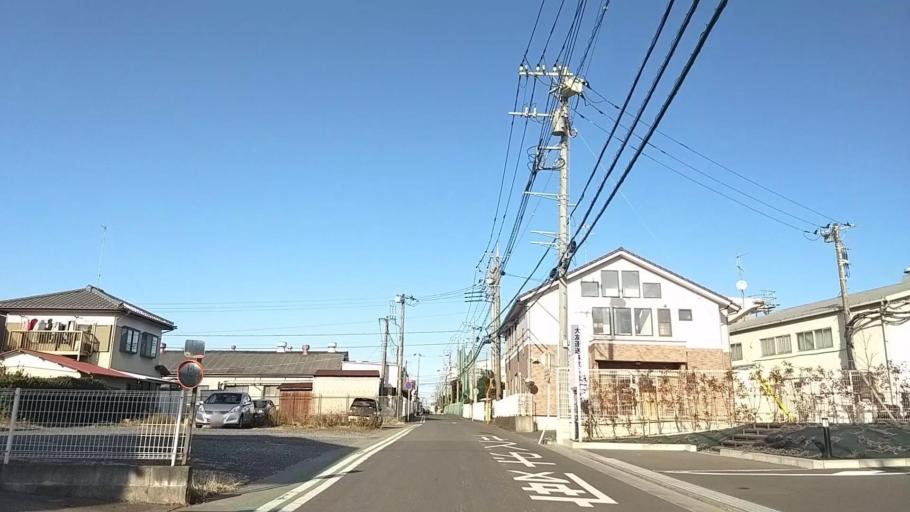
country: JP
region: Kanagawa
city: Atsugi
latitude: 35.4451
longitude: 139.3387
